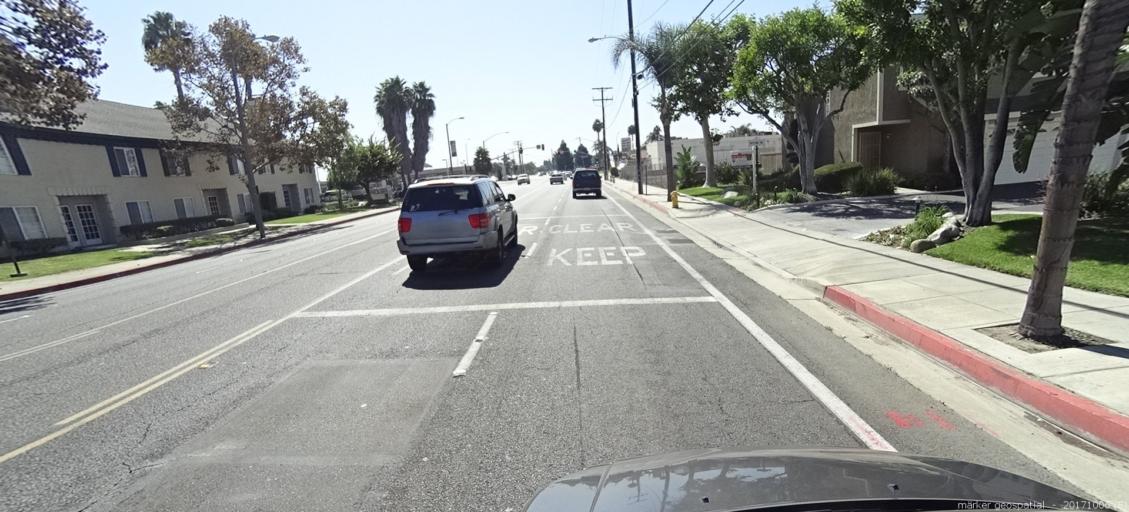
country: US
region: California
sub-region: Orange County
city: Stanton
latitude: 33.8041
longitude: -118.0020
